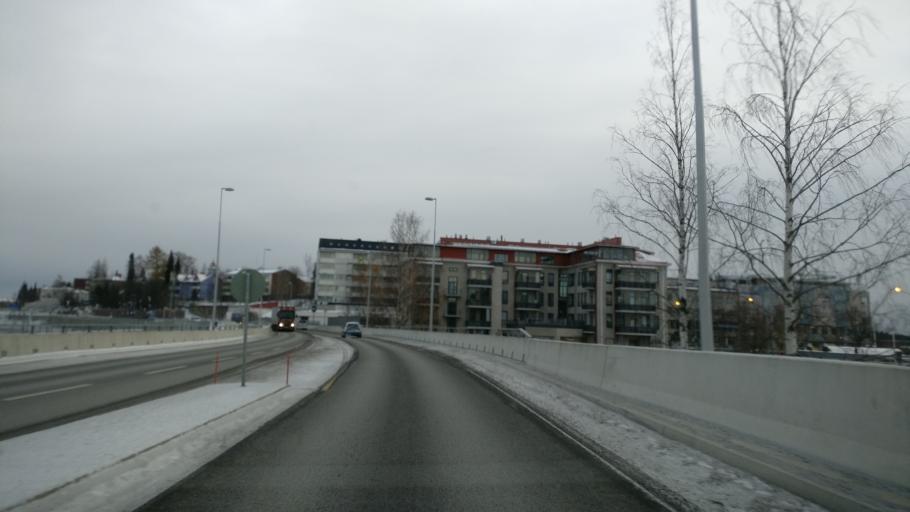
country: FI
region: Southern Savonia
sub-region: Savonlinna
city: Savonlinna
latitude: 61.8697
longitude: 28.8842
